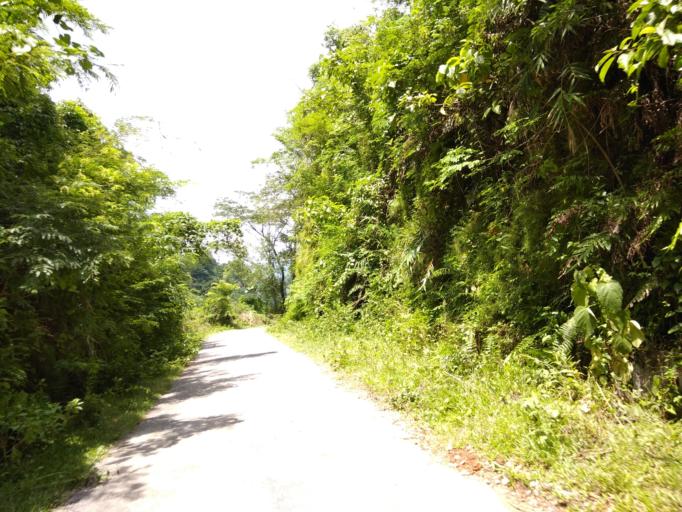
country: BD
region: Chittagong
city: Cox's Bazar
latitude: 21.6646
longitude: 92.3509
